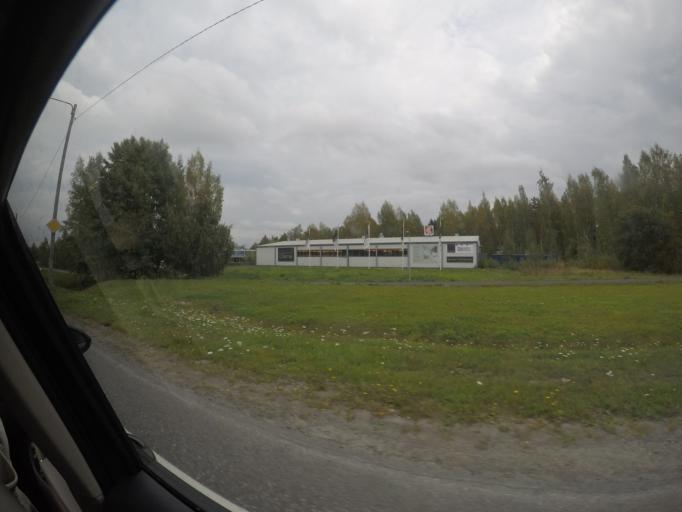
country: FI
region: Haeme
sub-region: Haemeenlinna
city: Haemeenlinna
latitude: 61.0177
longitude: 24.4205
